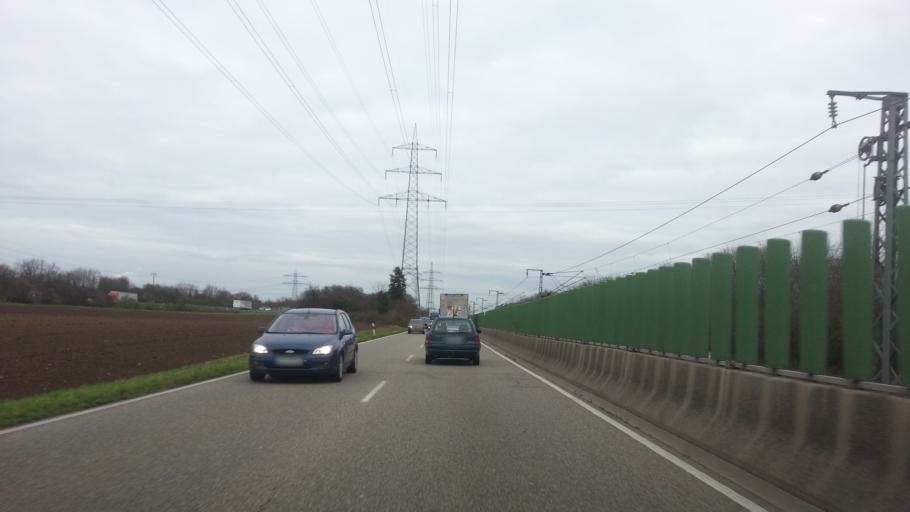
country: DE
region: Baden-Wuerttemberg
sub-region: Karlsruhe Region
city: Bruhl
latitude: 49.3876
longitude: 8.5453
